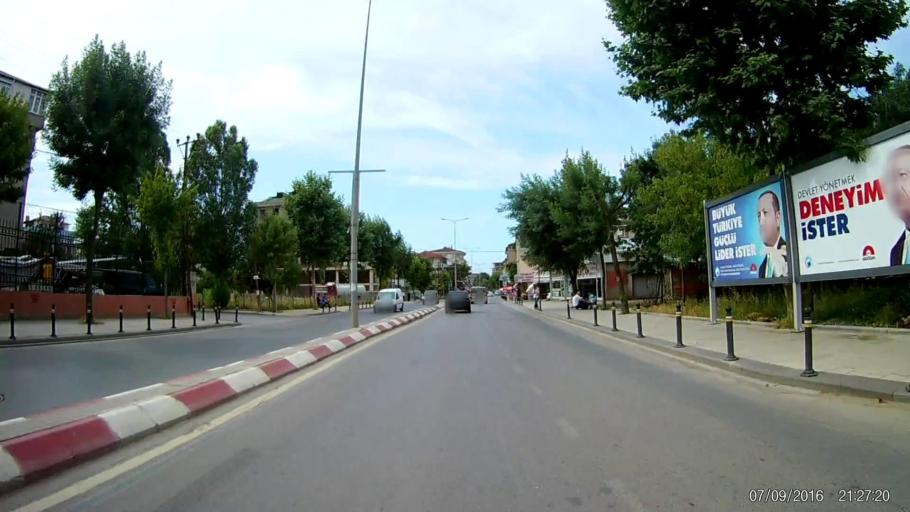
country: TR
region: Istanbul
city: Sultanbeyli
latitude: 40.9857
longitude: 29.2644
